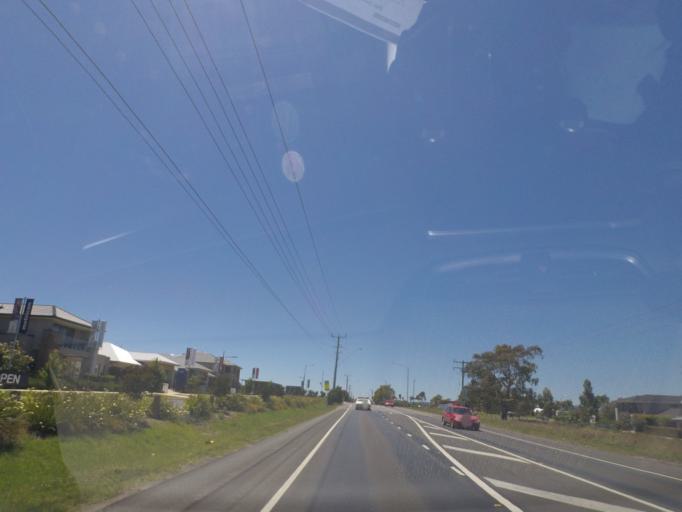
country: AU
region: Victoria
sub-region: Whittlesea
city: Epping
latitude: -37.6133
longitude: 145.0305
